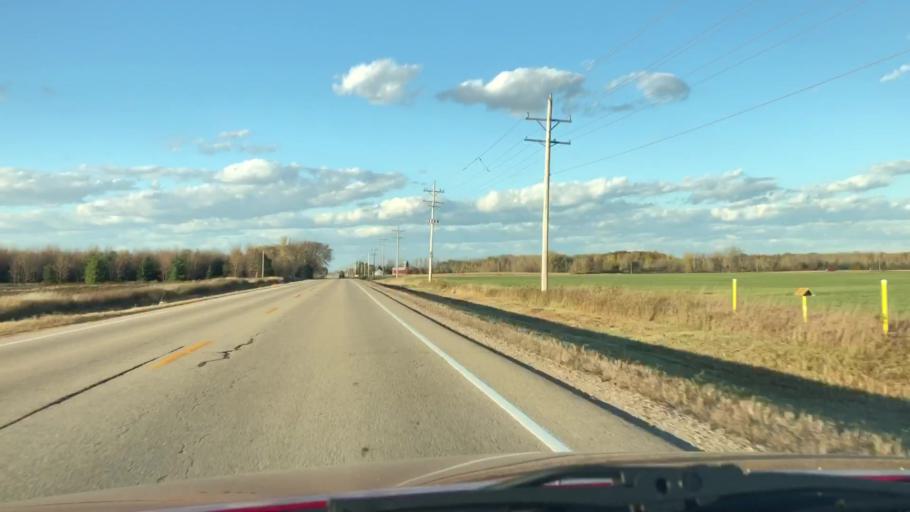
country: US
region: Wisconsin
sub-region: Outagamie County
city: Seymour
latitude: 44.4682
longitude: -88.2911
